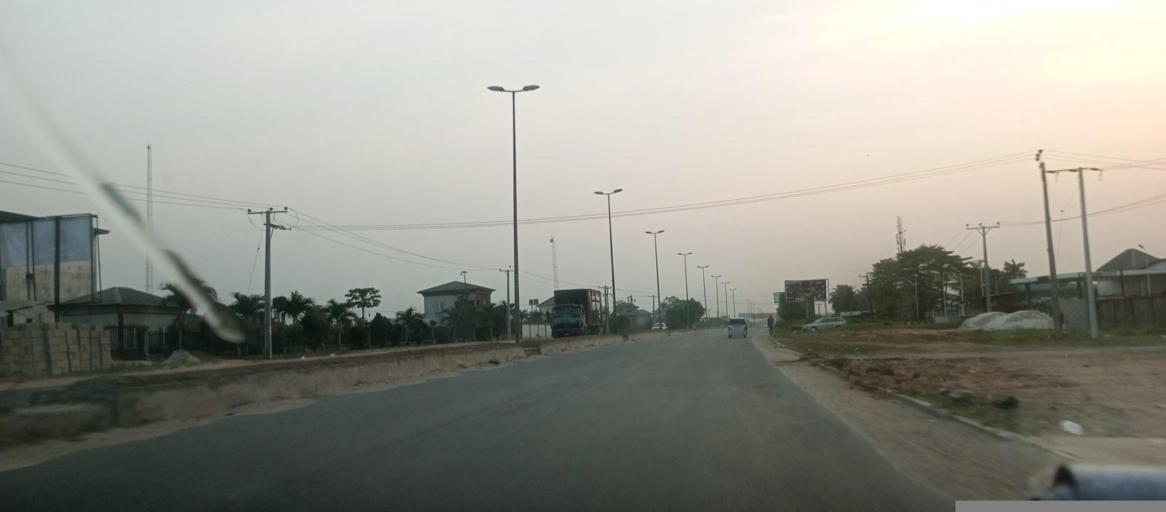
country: NG
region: Rivers
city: Emuoha
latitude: 4.9345
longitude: 7.0050
